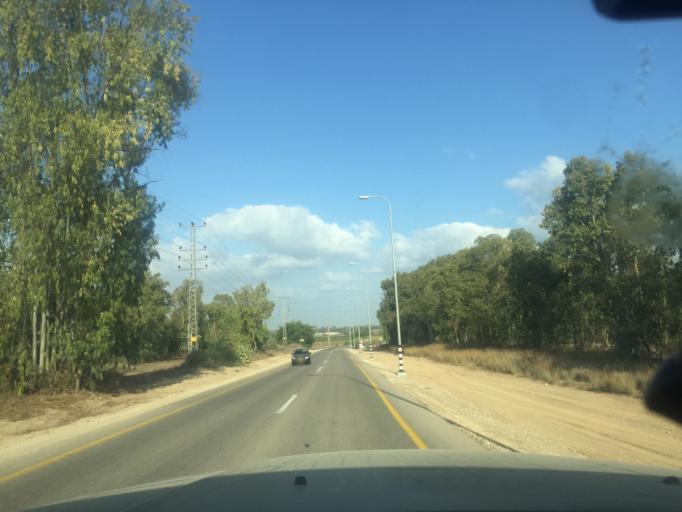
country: PS
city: Umm an Nasr
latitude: 31.6046
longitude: 34.5618
